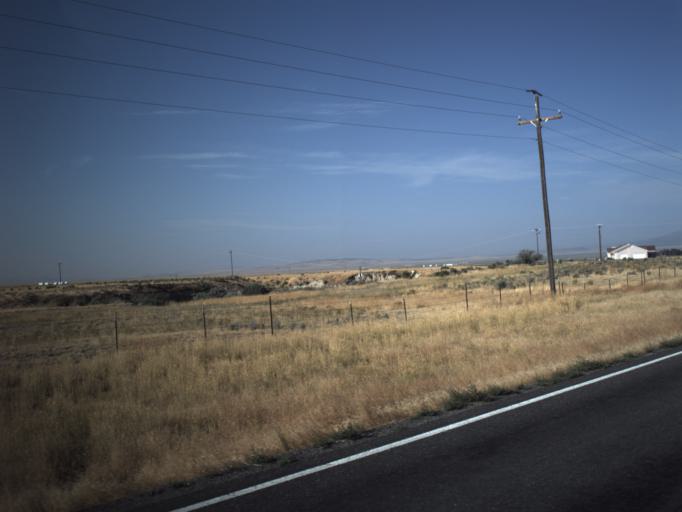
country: US
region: Idaho
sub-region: Oneida County
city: Malad City
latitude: 41.9675
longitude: -112.8113
